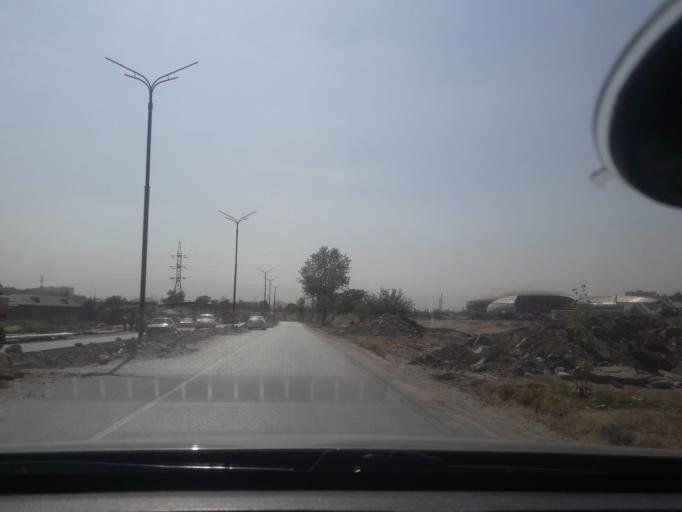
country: TJ
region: Dushanbe
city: Dushanbe
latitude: 38.6063
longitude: 68.7721
